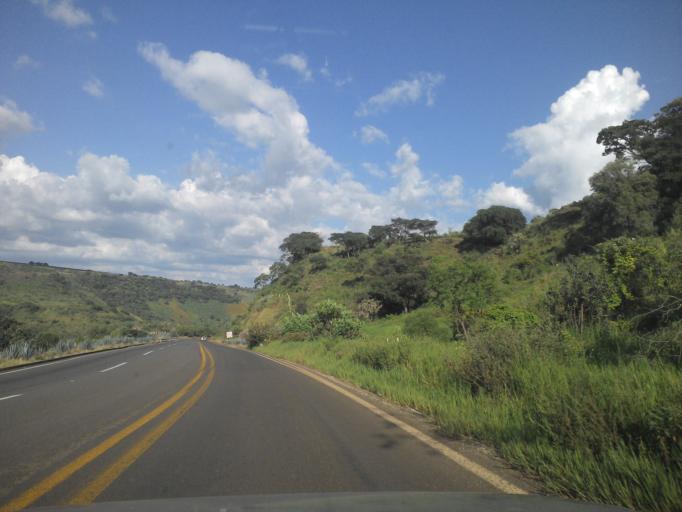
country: MX
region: Jalisco
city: Atotonilco el Alto
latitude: 20.5670
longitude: -102.5307
